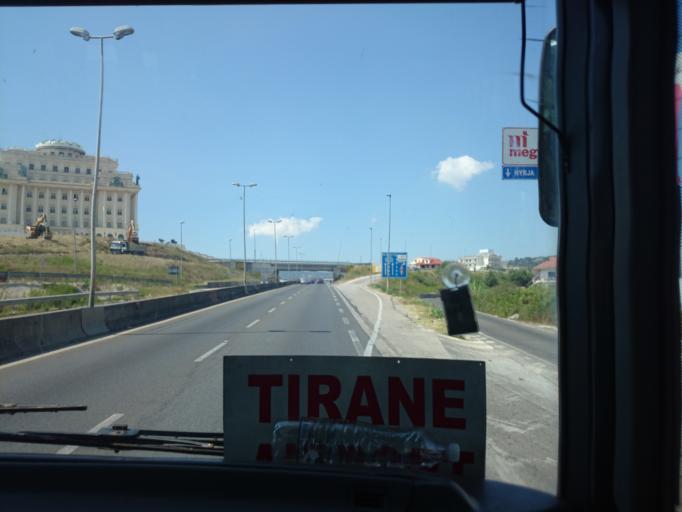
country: AL
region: Tirane
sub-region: Rrethi i Tiranes
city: Kashar
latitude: 41.3659
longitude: 19.7065
